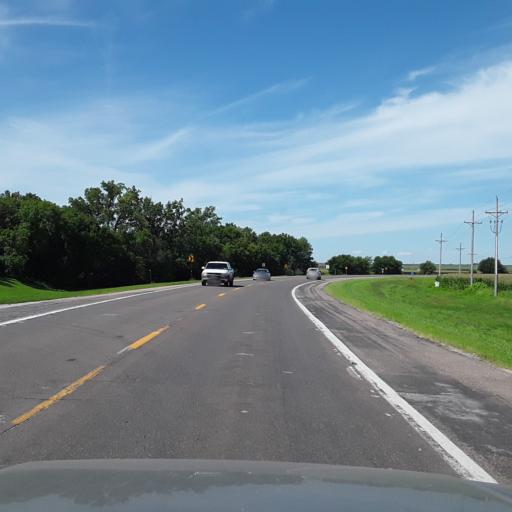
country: US
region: Nebraska
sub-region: Seward County
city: Seward
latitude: 40.9027
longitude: -97.1126
